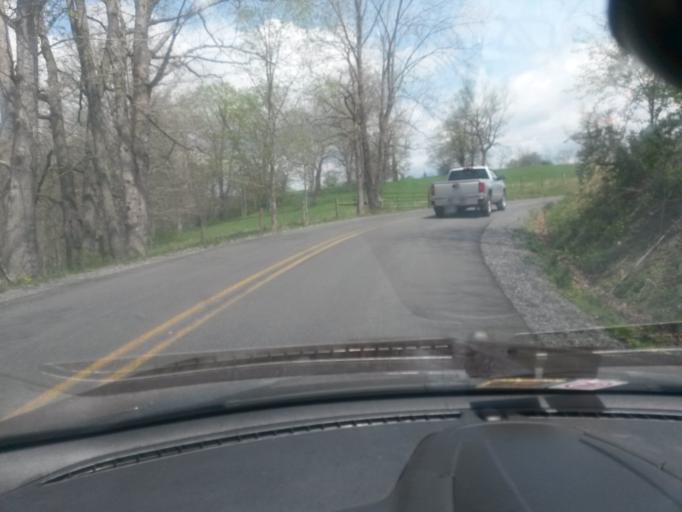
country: US
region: West Virginia
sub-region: Pocahontas County
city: Marlinton
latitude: 38.1107
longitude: -80.2178
